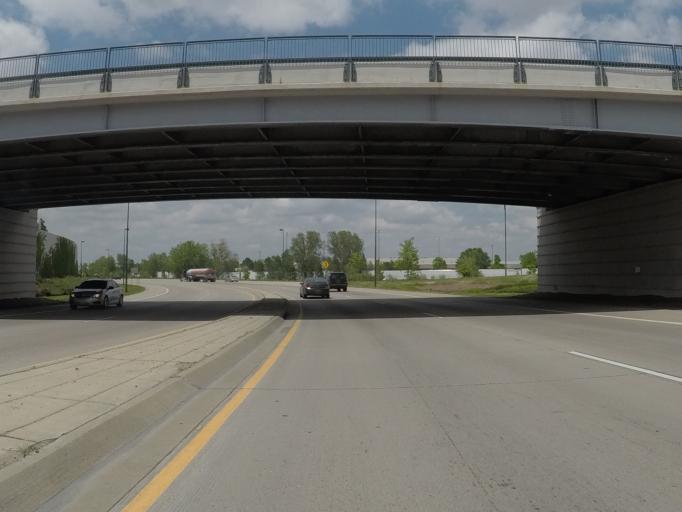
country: US
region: Colorado
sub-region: Adams County
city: Commerce City
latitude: 39.7853
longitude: -104.8997
